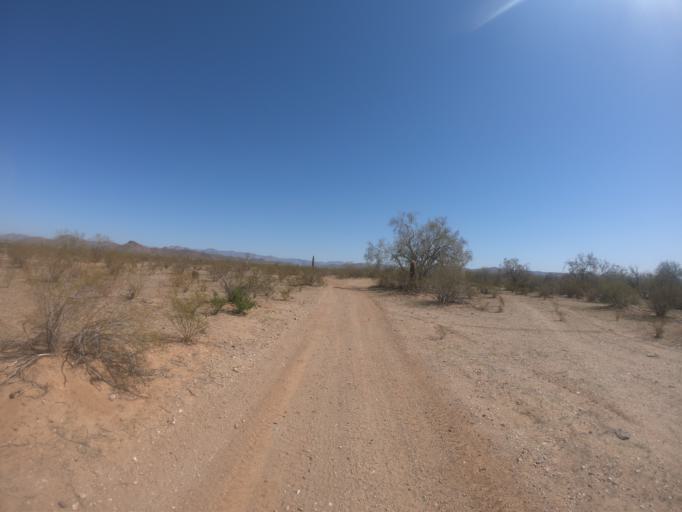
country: US
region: Arizona
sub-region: Pinal County
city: Gold Camp
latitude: 33.2379
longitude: -111.3357
